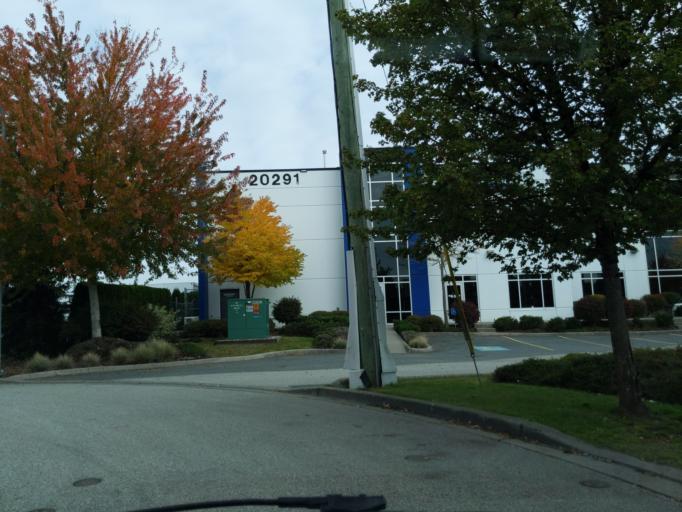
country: CA
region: British Columbia
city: Walnut Grove
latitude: 49.1871
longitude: -122.6596
